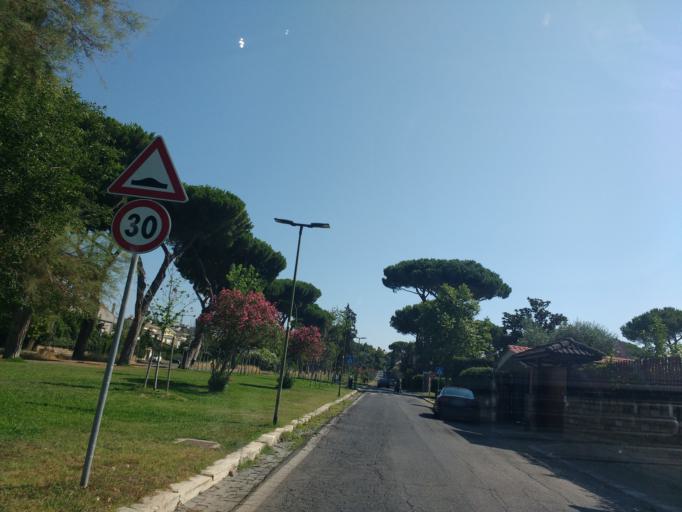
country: IT
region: Latium
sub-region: Citta metropolitana di Roma Capitale
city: Acilia-Castel Fusano-Ostia Antica
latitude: 41.7657
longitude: 12.3682
